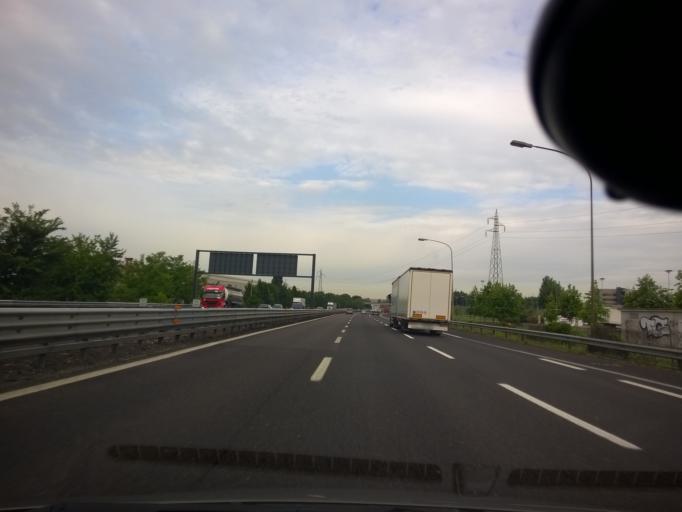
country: IT
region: Lombardy
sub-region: Provincia di Brescia
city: San Zeno Naviglio
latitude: 45.5066
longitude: 10.2286
